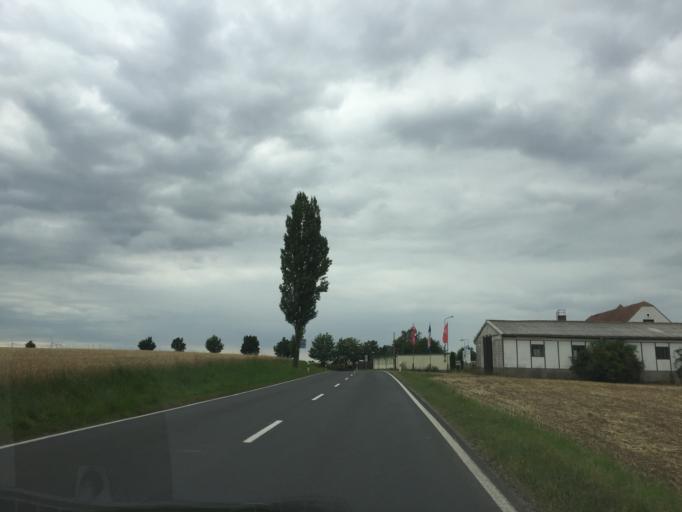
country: DE
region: Thuringia
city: Schmolln
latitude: 50.8733
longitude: 12.3727
